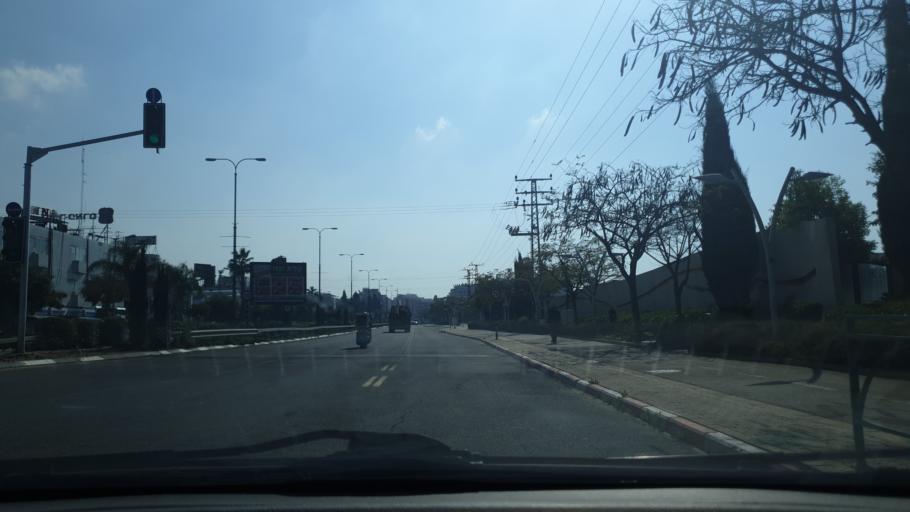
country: IL
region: Central District
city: Rishon LeZiyyon
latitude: 31.9774
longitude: 34.8080
